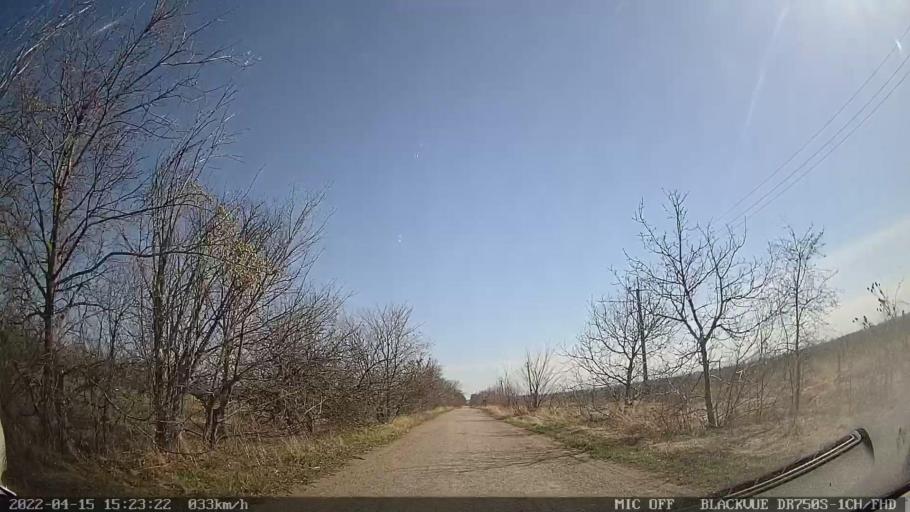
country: MD
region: Raionul Ocnita
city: Otaci
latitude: 48.3754
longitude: 27.9190
